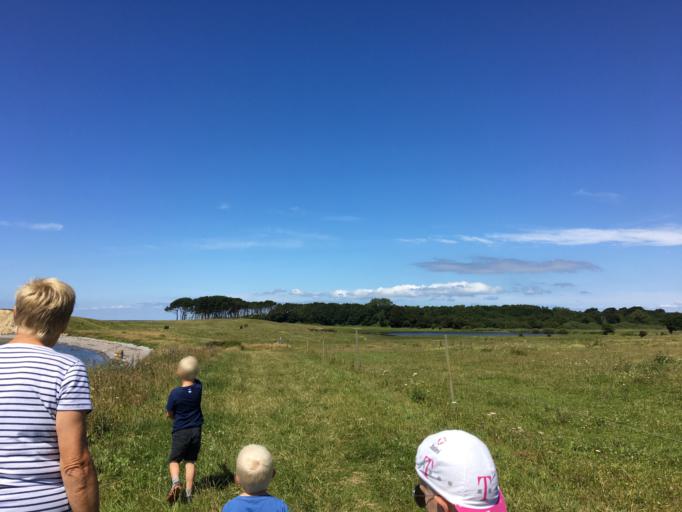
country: DK
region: South Denmark
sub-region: Langeland Kommune
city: Rudkobing
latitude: 54.7232
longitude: 10.6911
